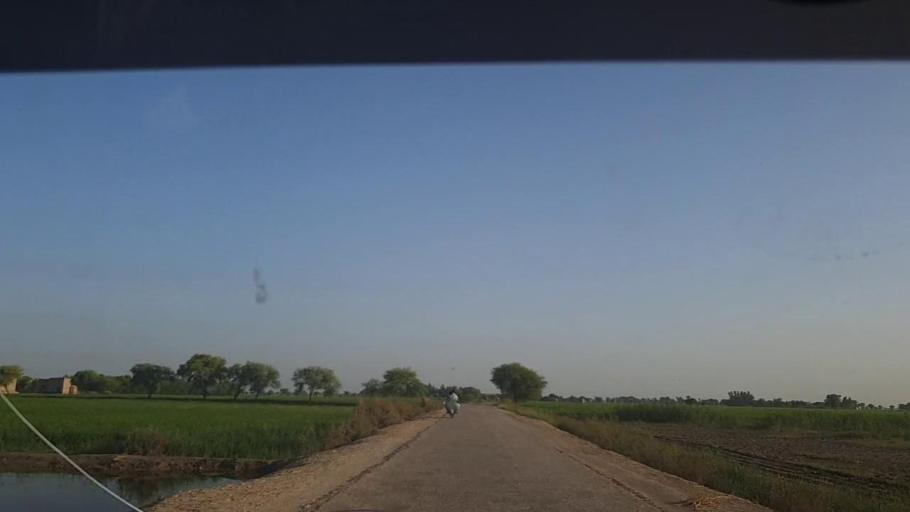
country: PK
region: Sindh
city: Thul
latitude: 28.2114
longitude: 68.8700
